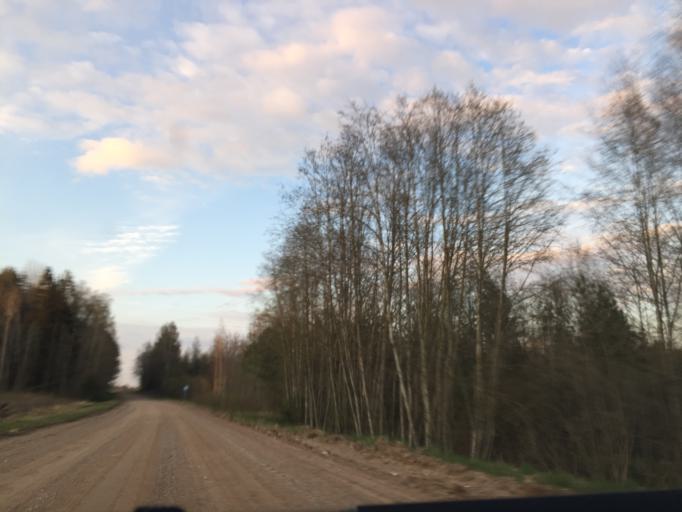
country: LV
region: Gulbenes Rajons
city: Gulbene
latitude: 57.2280
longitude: 26.7965
